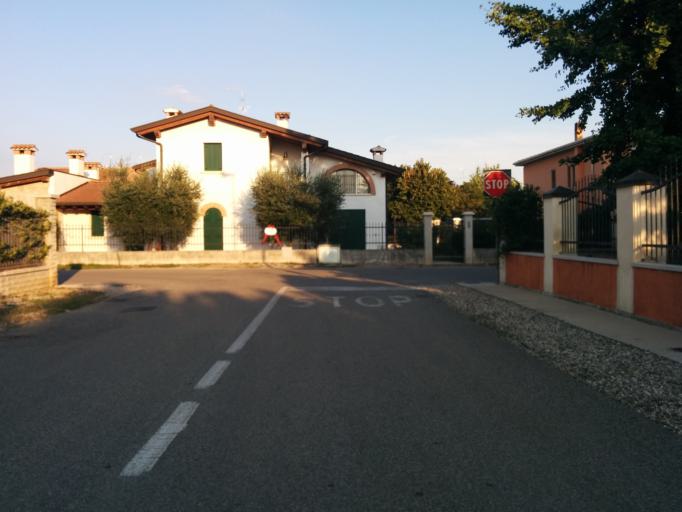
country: IT
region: Veneto
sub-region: Provincia di Verona
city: Quaderni
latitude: 45.3272
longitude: 10.7888
